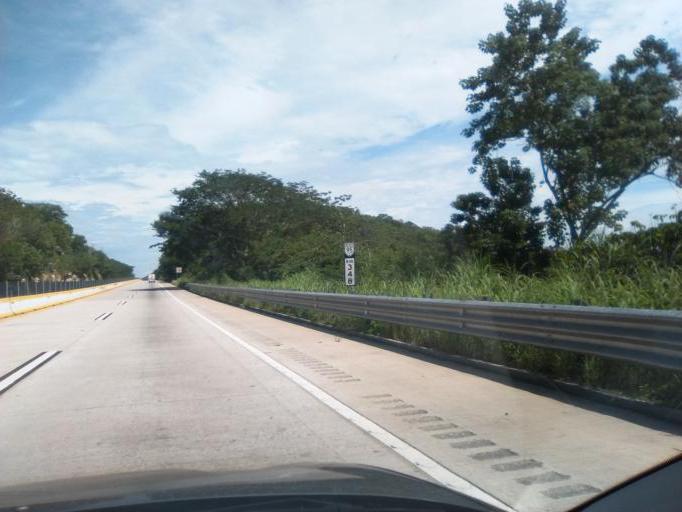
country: MX
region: Guerrero
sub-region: Acapulco de Juarez
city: Kilometro 30
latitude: 17.0026
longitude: -99.6774
